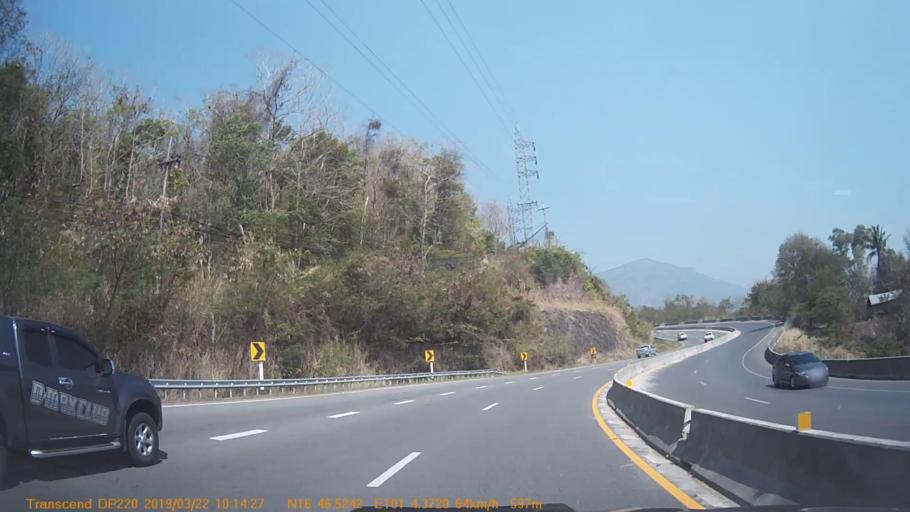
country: TH
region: Phetchabun
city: Khao Kho
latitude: 16.7759
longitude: 101.0721
